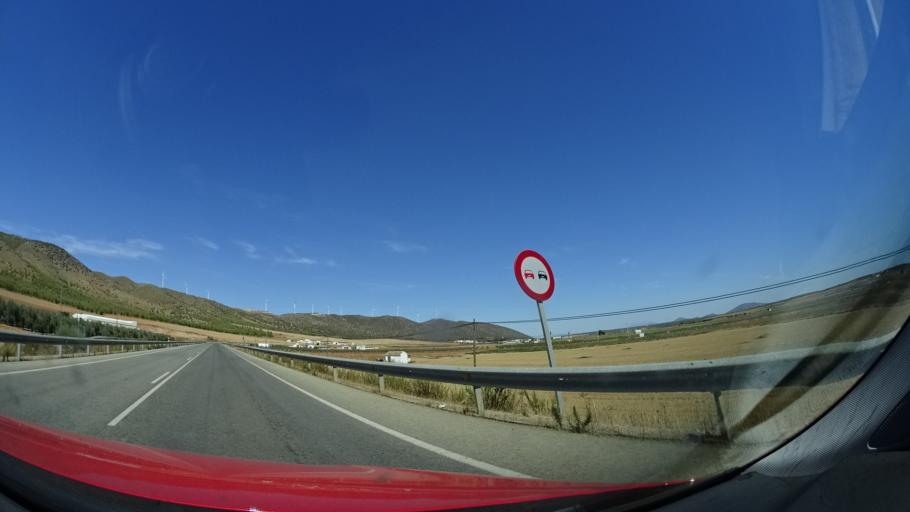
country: ES
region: Andalusia
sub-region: Provincia de Malaga
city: Sierra de Yeguas
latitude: 37.1427
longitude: -4.8580
